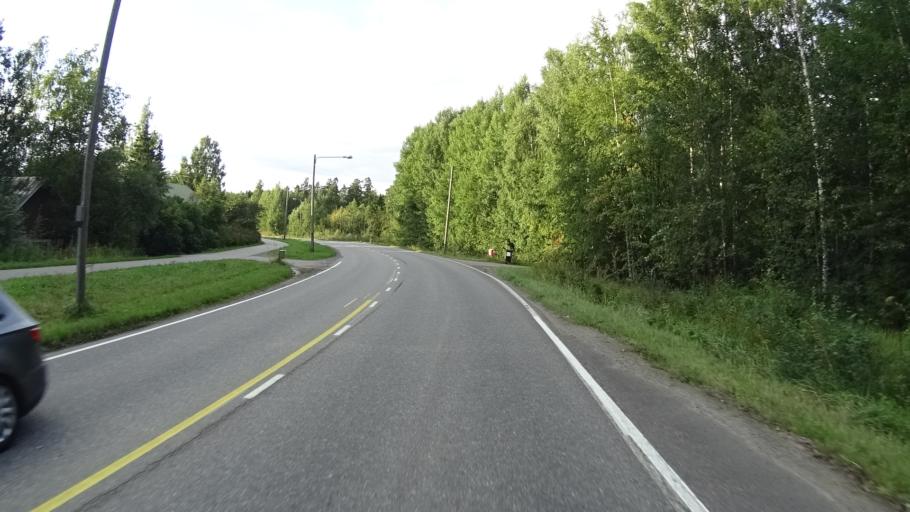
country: FI
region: Uusimaa
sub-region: Helsinki
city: Kilo
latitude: 60.3230
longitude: 24.8691
